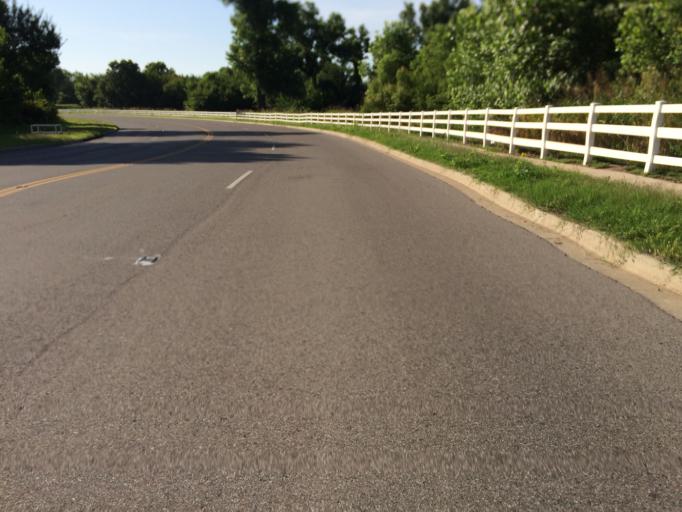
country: US
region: Oklahoma
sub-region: Cleveland County
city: Norman
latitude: 35.2045
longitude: -97.4885
